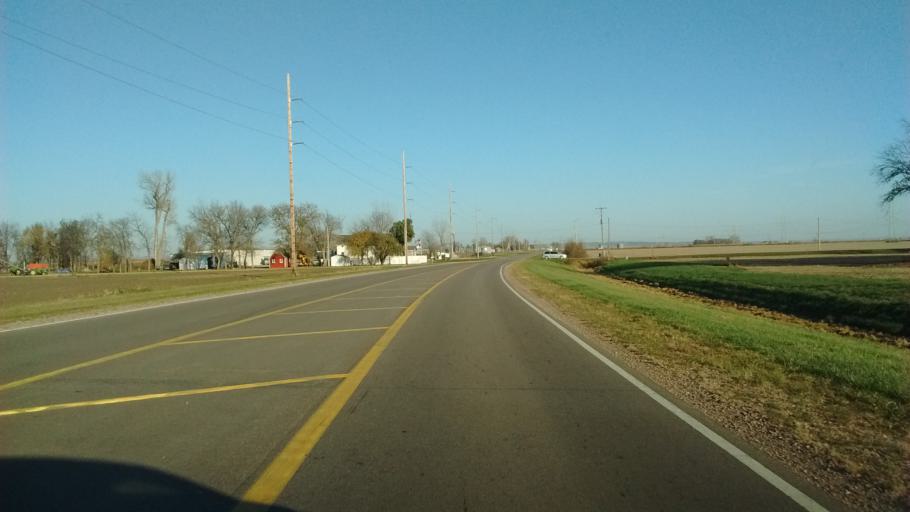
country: US
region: Iowa
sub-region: Woodbury County
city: Sergeant Bluff
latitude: 42.3301
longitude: -96.3123
